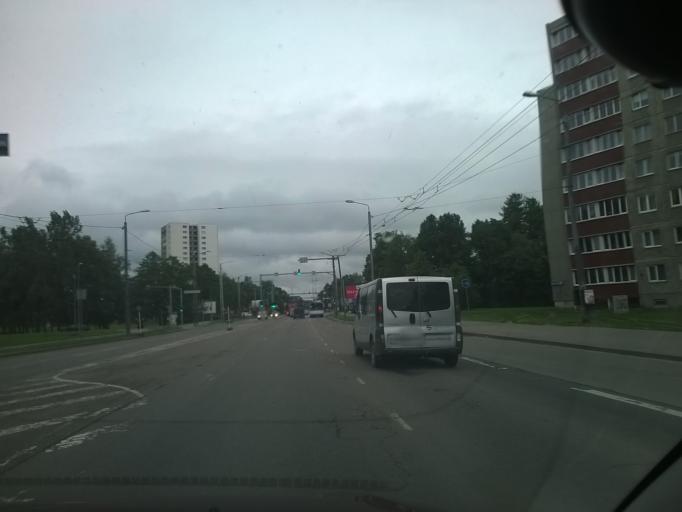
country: EE
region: Harju
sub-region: Tallinna linn
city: Tallinn
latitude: 59.4106
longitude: 24.6871
